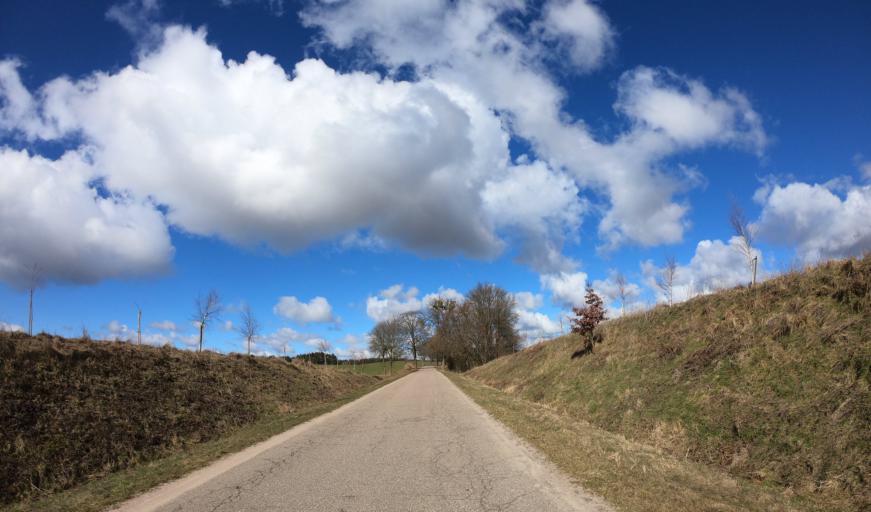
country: PL
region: West Pomeranian Voivodeship
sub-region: Powiat drawski
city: Zlocieniec
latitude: 53.4660
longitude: 15.9322
